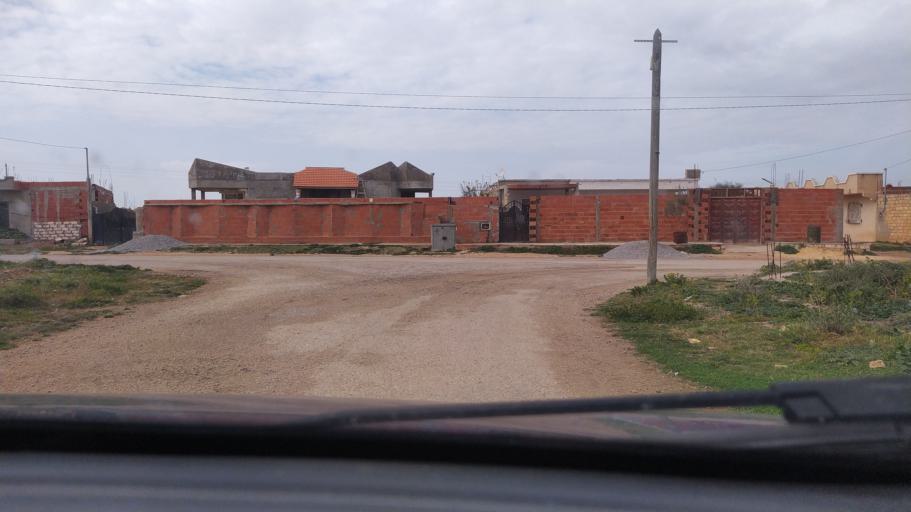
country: TN
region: Al Munastir
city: Sidi Bin Nur
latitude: 35.5188
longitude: 10.9277
